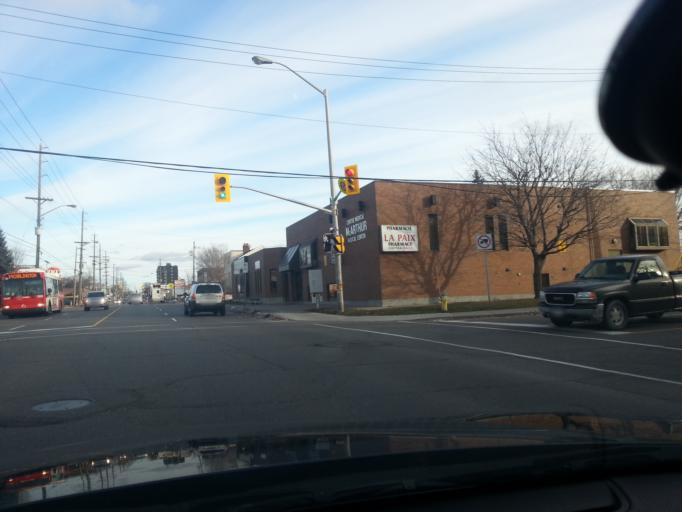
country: CA
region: Ontario
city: Ottawa
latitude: 45.4320
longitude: -75.6508
